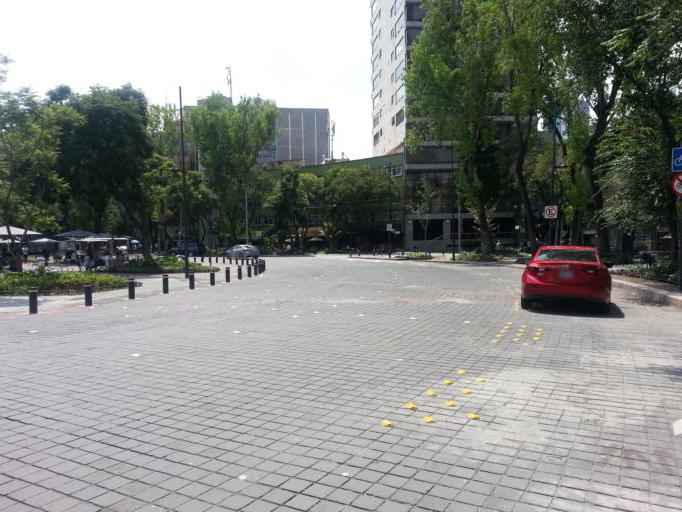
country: MX
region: Mexico City
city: Benito Juarez
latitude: 19.4204
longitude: -99.1662
